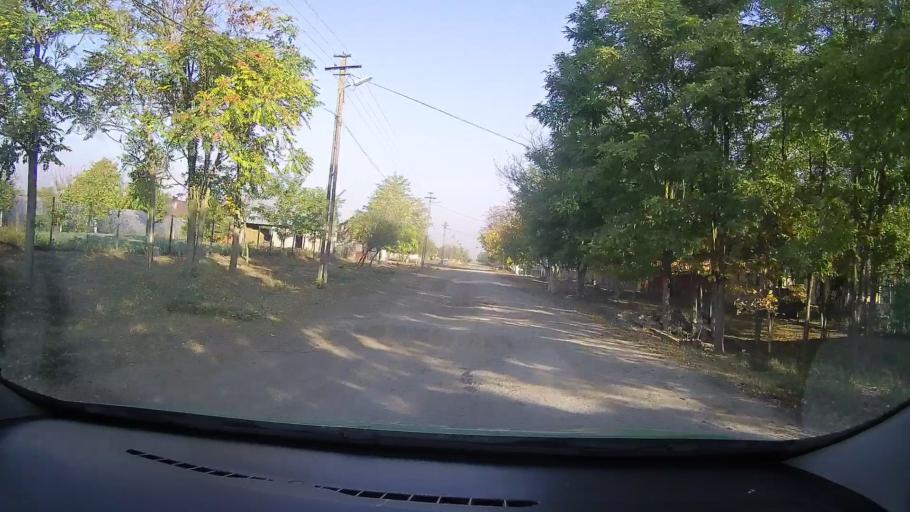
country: RO
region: Arad
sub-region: Comuna Graniceri
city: Graniceri
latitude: 46.5247
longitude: 21.3108
